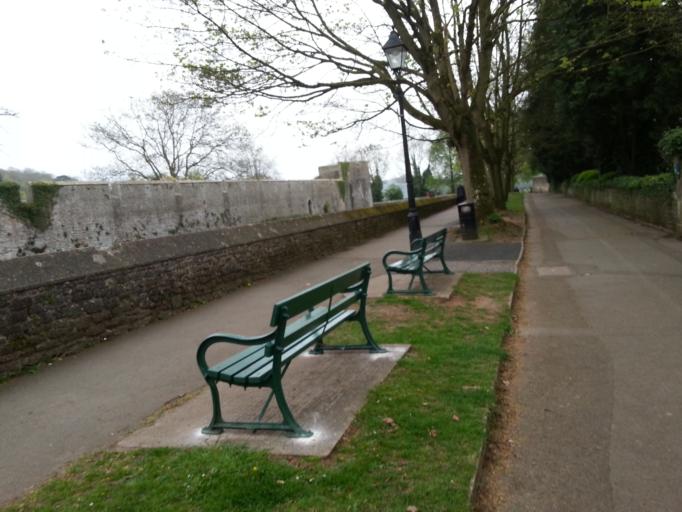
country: GB
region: England
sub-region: Somerset
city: Wells
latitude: 51.2085
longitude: -2.6439
